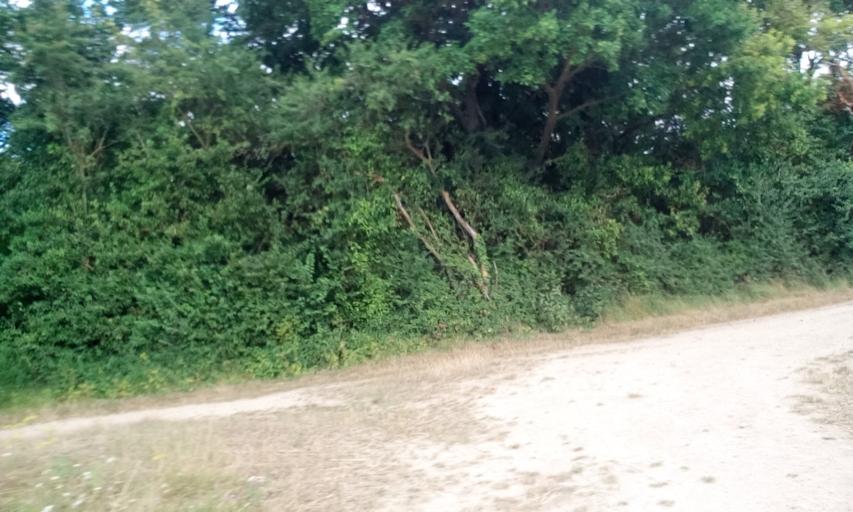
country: FR
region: Lower Normandy
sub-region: Departement du Calvados
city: Bellengreville
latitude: 49.1134
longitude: -0.1972
